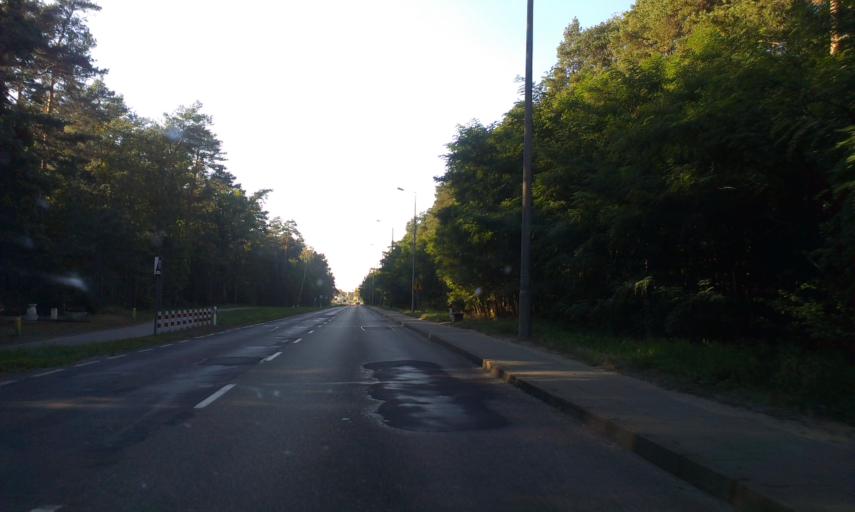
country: PL
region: Kujawsko-Pomorskie
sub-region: Powiat tucholski
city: Tuchola
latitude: 53.5734
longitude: 17.8849
